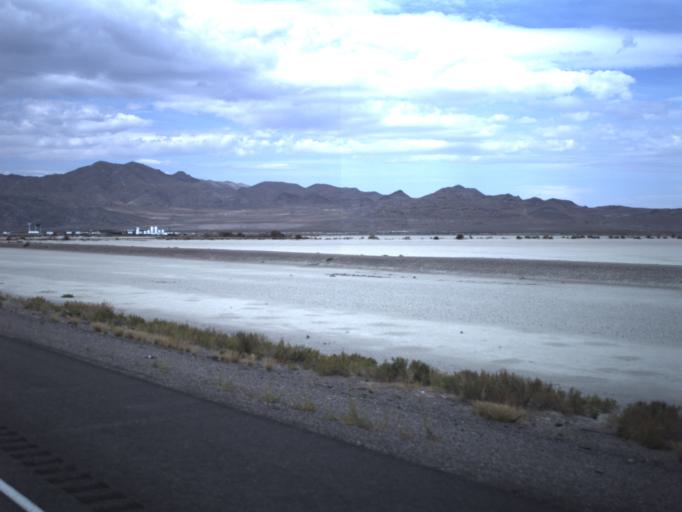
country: US
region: Utah
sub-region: Tooele County
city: Wendover
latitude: 40.7415
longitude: -113.9575
